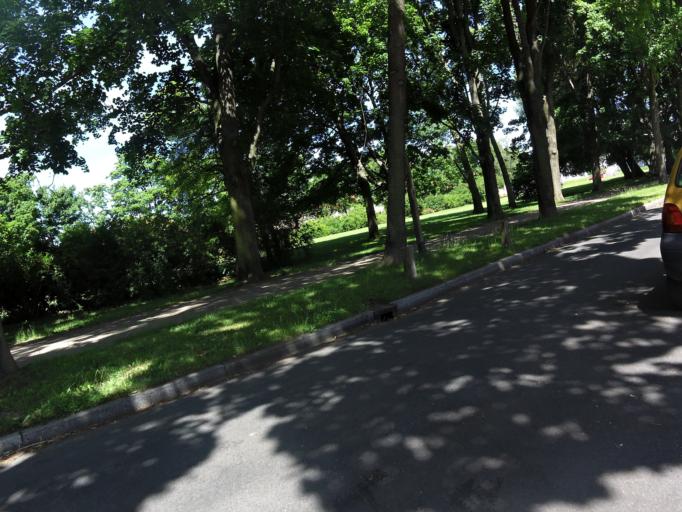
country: DE
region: Saxony
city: Markkleeberg
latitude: 51.3055
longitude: 12.3987
